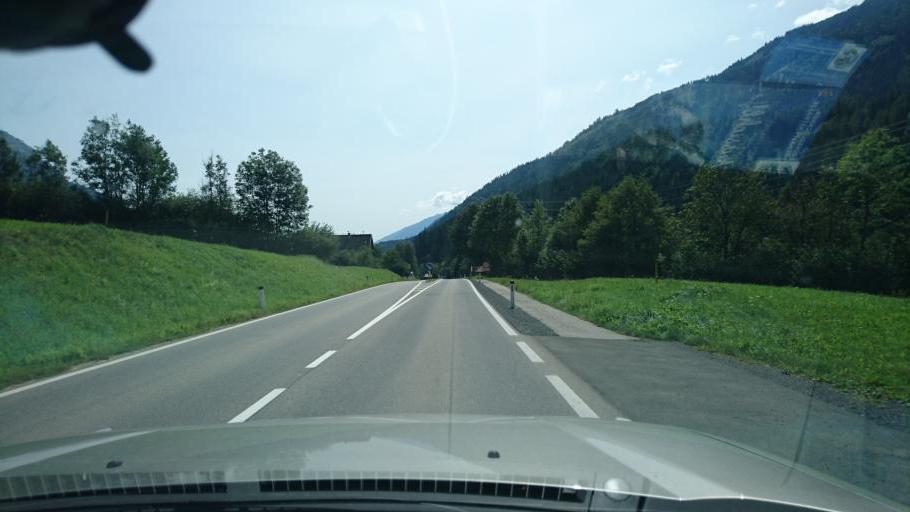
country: AT
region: Carinthia
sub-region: Politischer Bezirk Spittal an der Drau
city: Muhldorf
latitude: 46.8792
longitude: 13.2944
